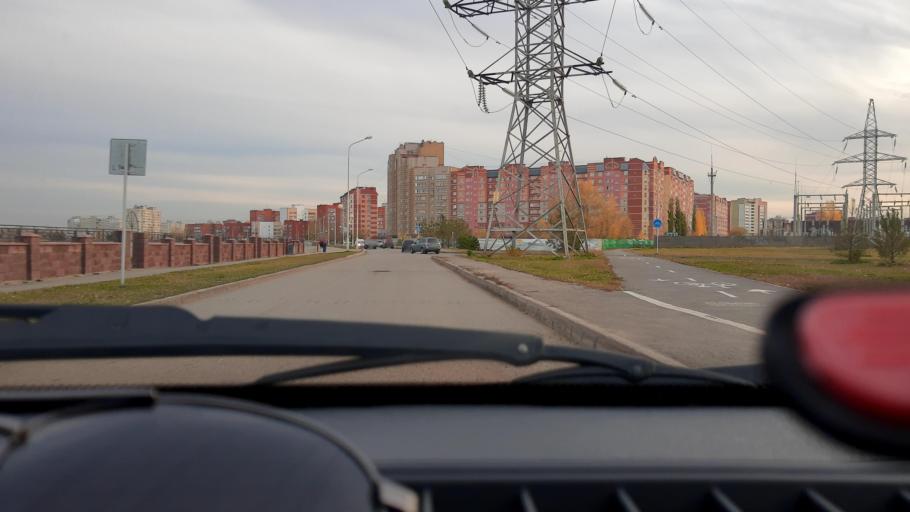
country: RU
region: Bashkortostan
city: Ufa
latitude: 54.7831
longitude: 56.0777
